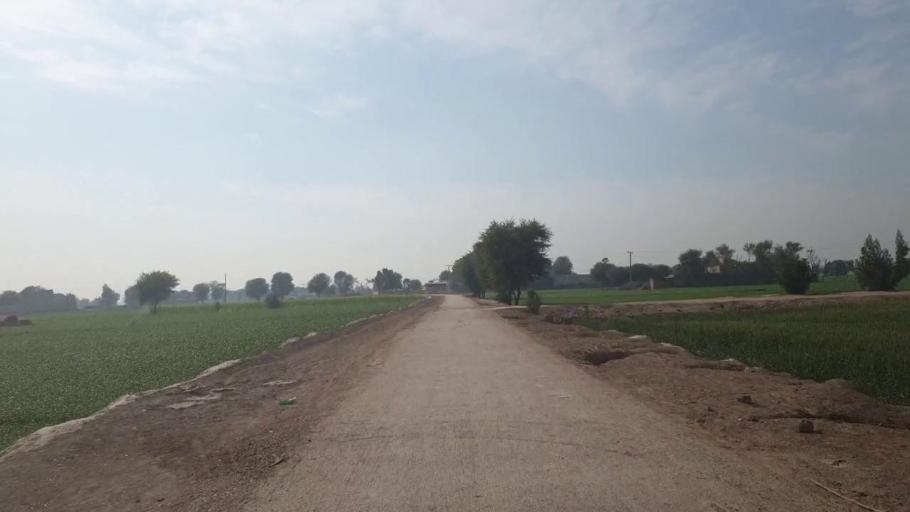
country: PK
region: Sindh
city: Nawabshah
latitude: 26.1629
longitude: 68.5028
